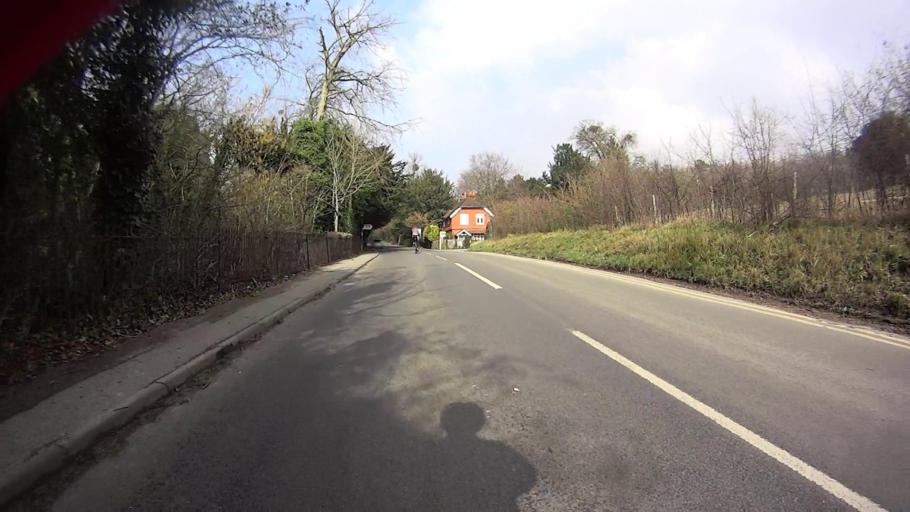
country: GB
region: England
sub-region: Surrey
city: Mickleham
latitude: 51.2574
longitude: -0.3228
